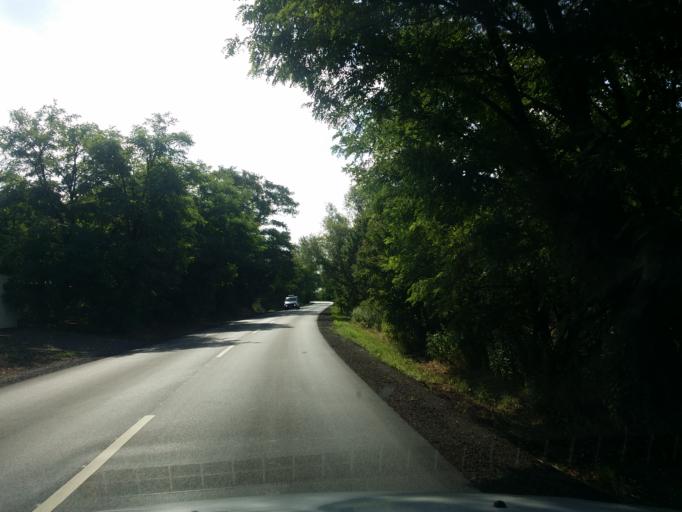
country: HU
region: Heves
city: Heves
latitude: 47.6256
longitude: 20.2406
